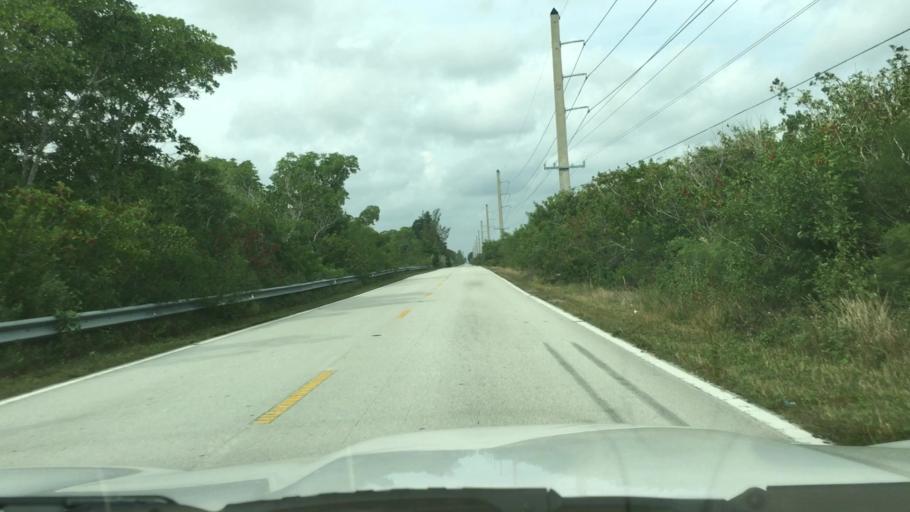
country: US
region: Florida
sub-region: Monroe County
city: North Key Largo
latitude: 25.3286
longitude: -80.4049
